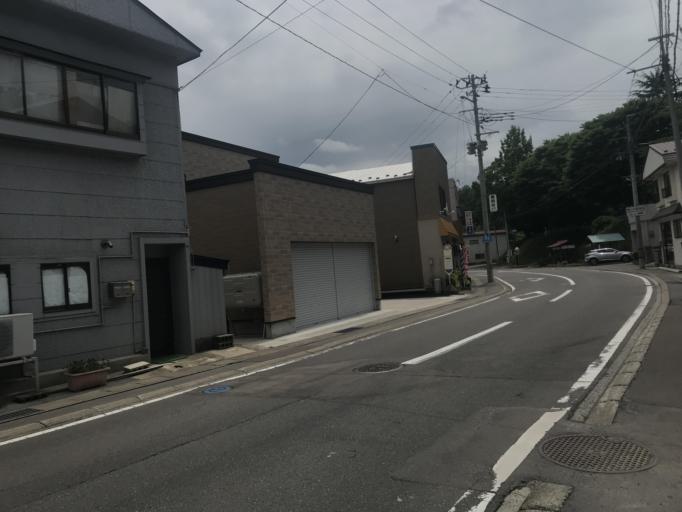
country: JP
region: Aomori
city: Shimokizukuri
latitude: 40.7803
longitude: 140.2063
